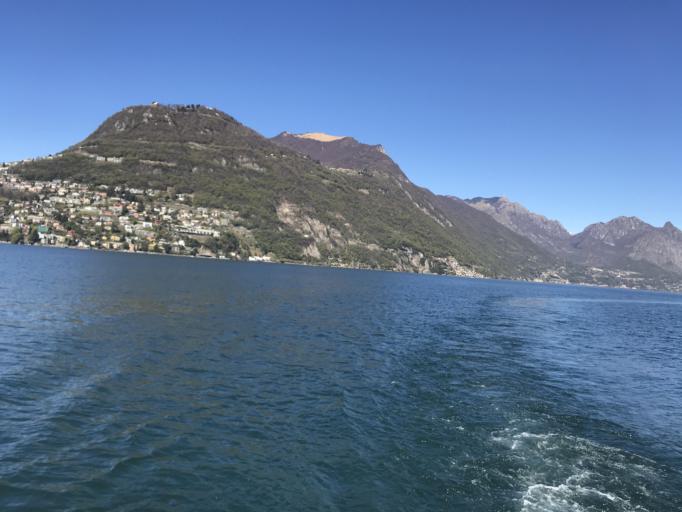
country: IT
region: Lombardy
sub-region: Provincia di Como
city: Campione
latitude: 45.9864
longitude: 8.9807
